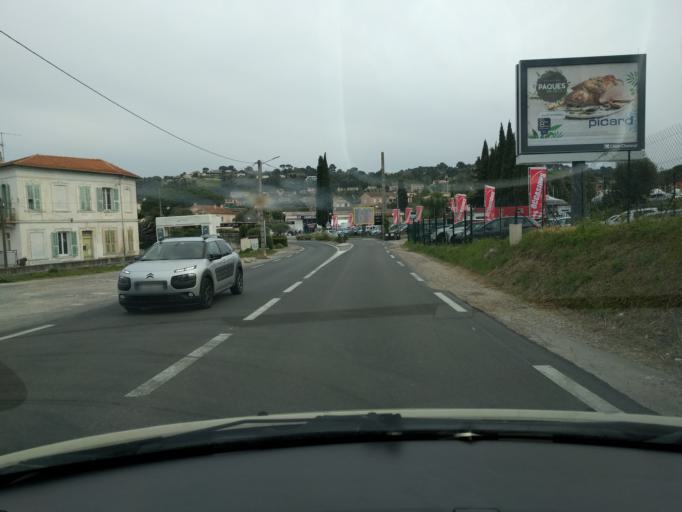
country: FR
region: Provence-Alpes-Cote d'Azur
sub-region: Departement des Alpes-Maritimes
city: La Roquette-sur-Siagne
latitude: 43.5761
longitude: 6.9519
